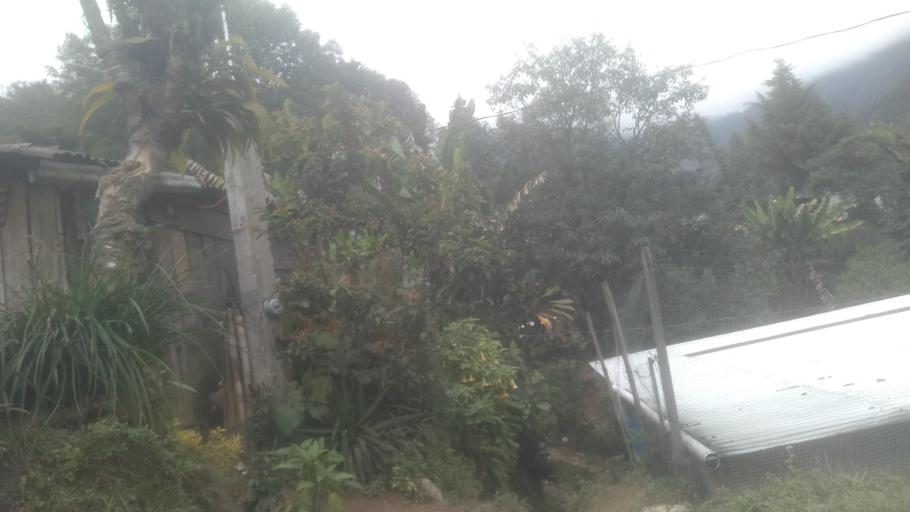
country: MX
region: Veracruz
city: Chocaman
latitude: 18.9955
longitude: -97.0591
